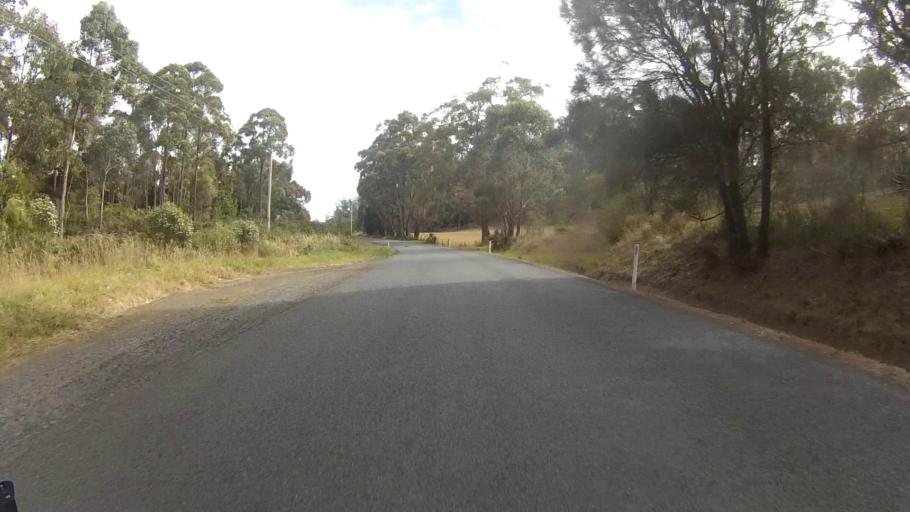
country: AU
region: Tasmania
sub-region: Sorell
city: Sorell
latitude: -42.8109
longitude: 147.7941
